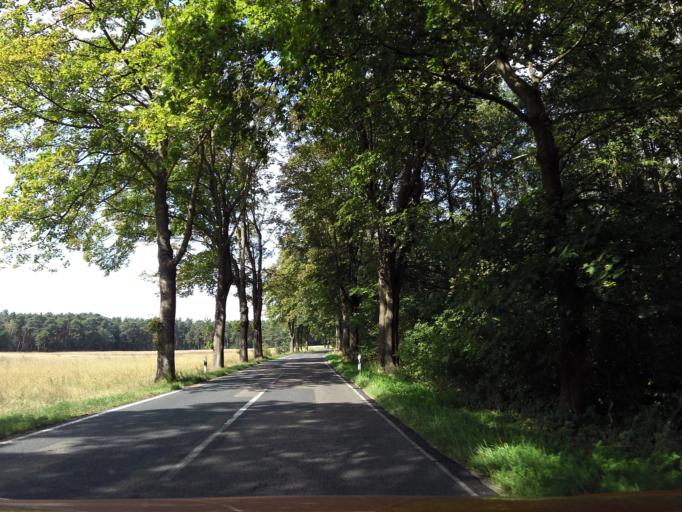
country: DE
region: Brandenburg
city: Michendorf
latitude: 52.2815
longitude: 13.1142
